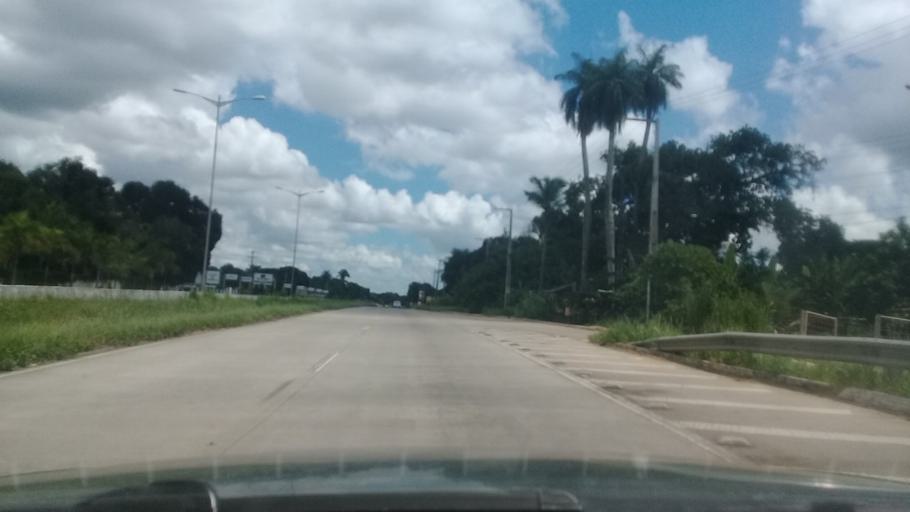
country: BR
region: Pernambuco
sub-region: Sao Lourenco Da Mata
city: Sao Lourenco da Mata
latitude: -7.9337
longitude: -35.1314
